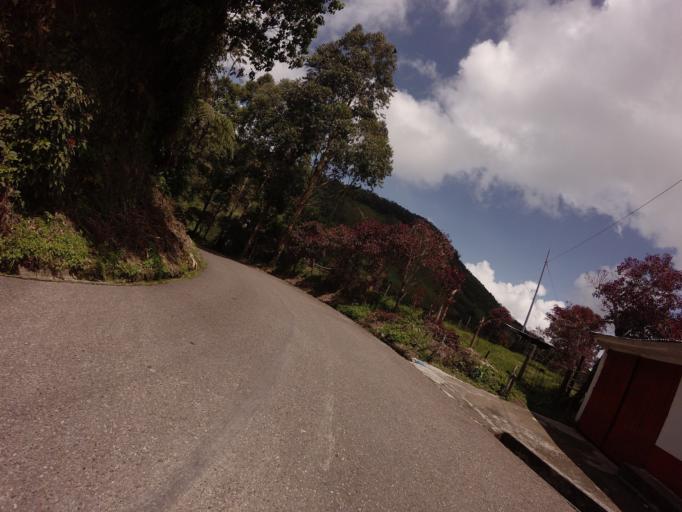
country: CO
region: Caldas
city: Marquetalia
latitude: 5.2734
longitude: -75.1102
